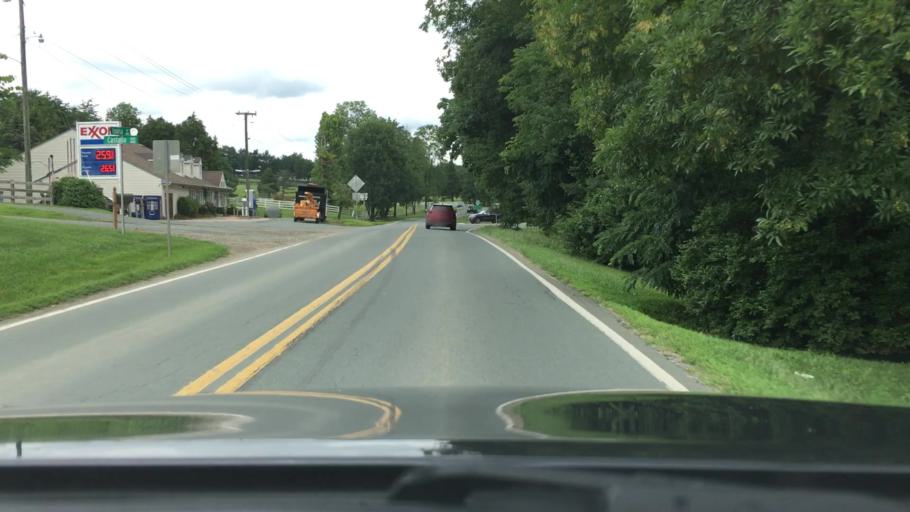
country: US
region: Virginia
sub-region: Fluvanna County
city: Lake Monticello
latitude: 38.0535
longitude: -78.3187
